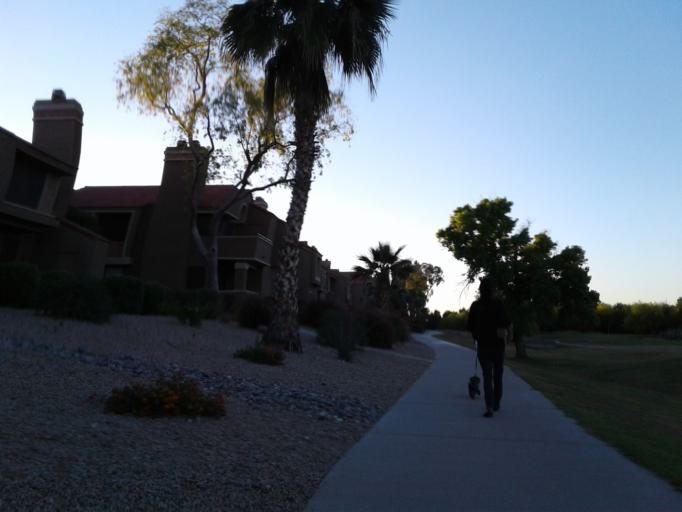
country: US
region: Arizona
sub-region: Maricopa County
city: Paradise Valley
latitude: 33.5844
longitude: -111.9714
